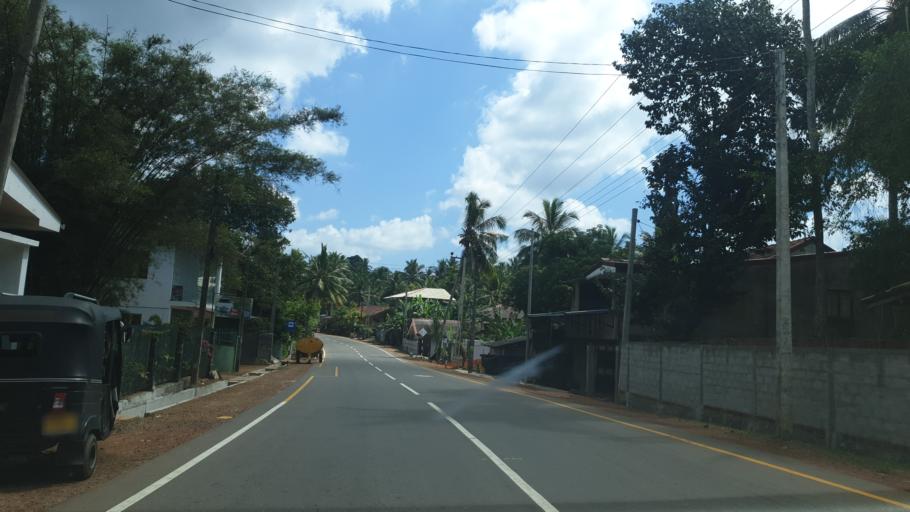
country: LK
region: Western
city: Panadura
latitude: 6.6647
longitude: 79.9516
